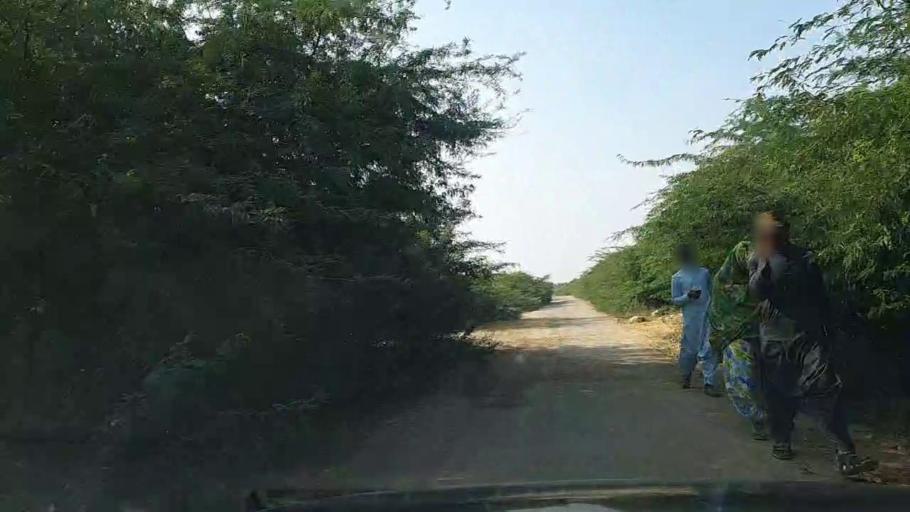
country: PK
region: Sindh
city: Gharo
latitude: 24.7582
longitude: 67.5261
